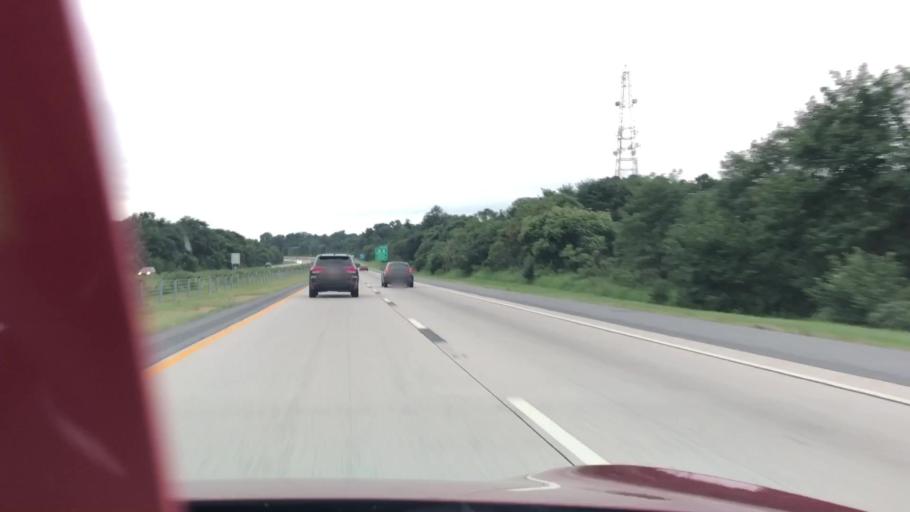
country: US
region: Delaware
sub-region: New Castle County
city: Middletown
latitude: 39.4623
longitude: -75.6617
